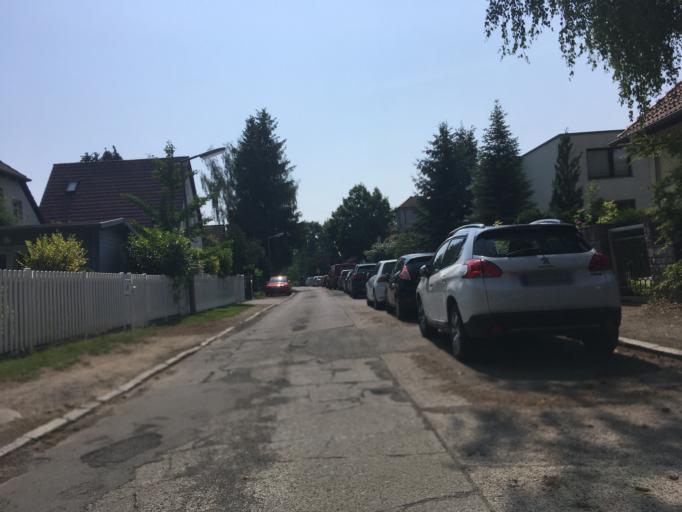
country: DE
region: Berlin
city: Heiligensee
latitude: 52.6162
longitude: 13.2222
